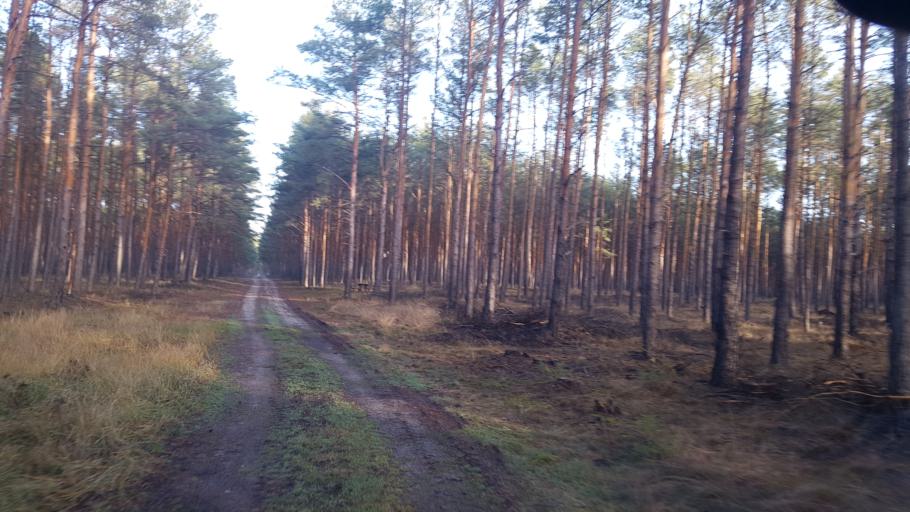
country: DE
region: Brandenburg
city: Schilda
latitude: 51.6249
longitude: 13.3923
